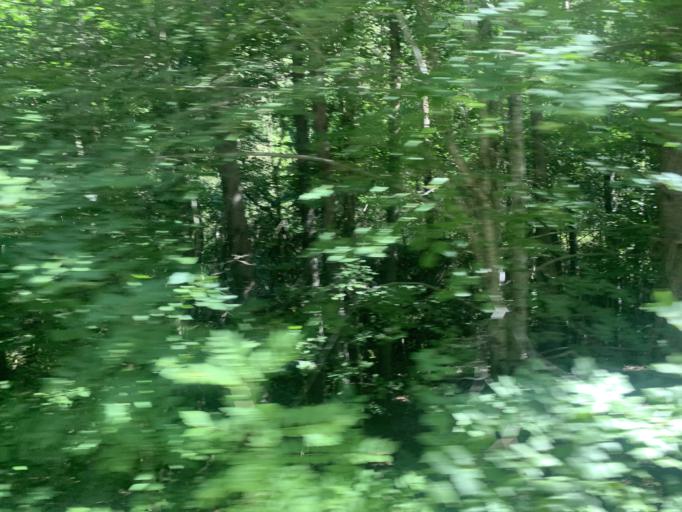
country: ES
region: Aragon
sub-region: Provincia de Huesca
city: Broto
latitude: 42.6537
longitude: -0.0948
